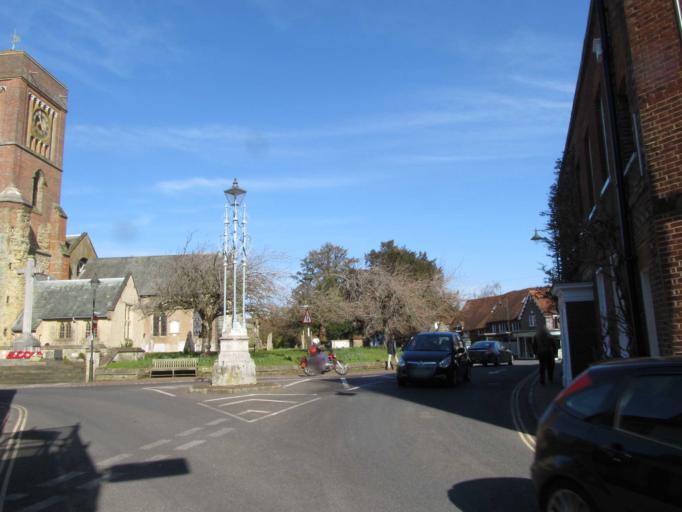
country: GB
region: England
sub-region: West Sussex
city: Petworth
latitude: 50.9874
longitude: -0.6092
